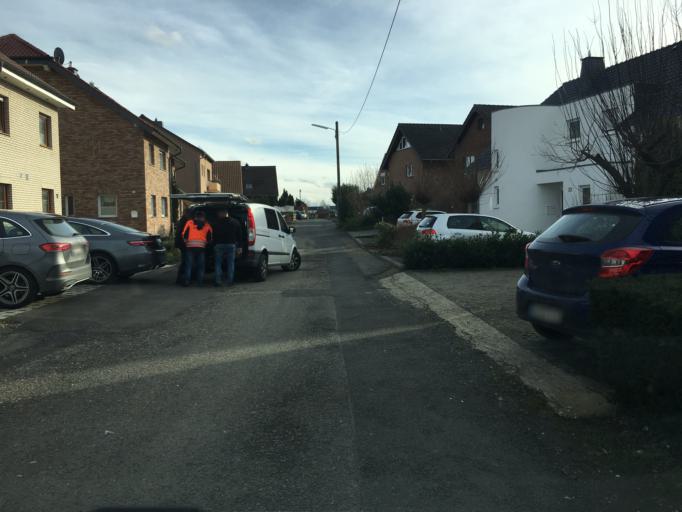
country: DE
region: North Rhine-Westphalia
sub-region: Regierungsbezirk Koln
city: Alfter
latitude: 50.7671
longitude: 7.0465
